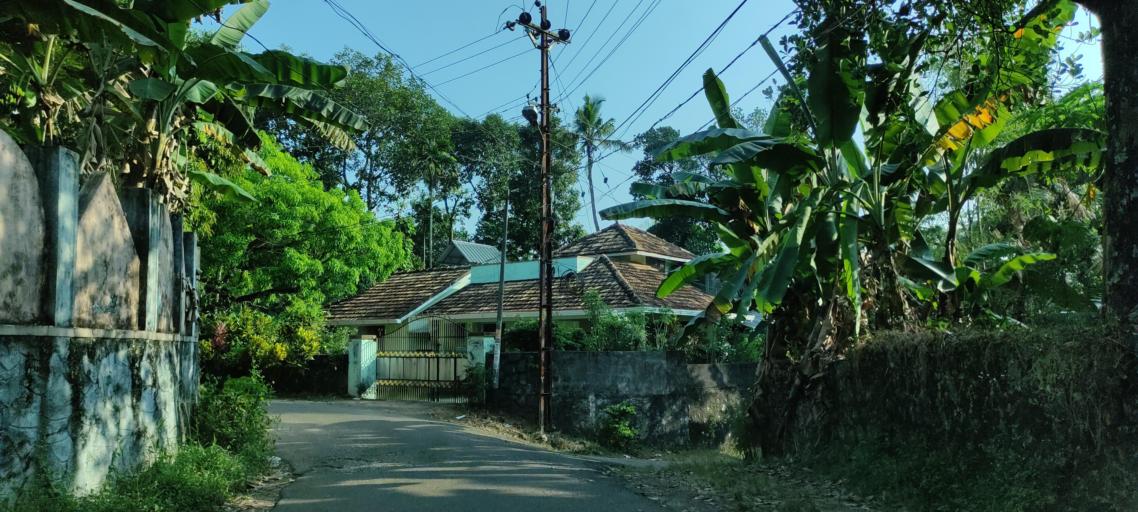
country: IN
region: Kerala
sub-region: Pattanamtitta
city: Adur
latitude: 9.1568
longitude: 76.7425
